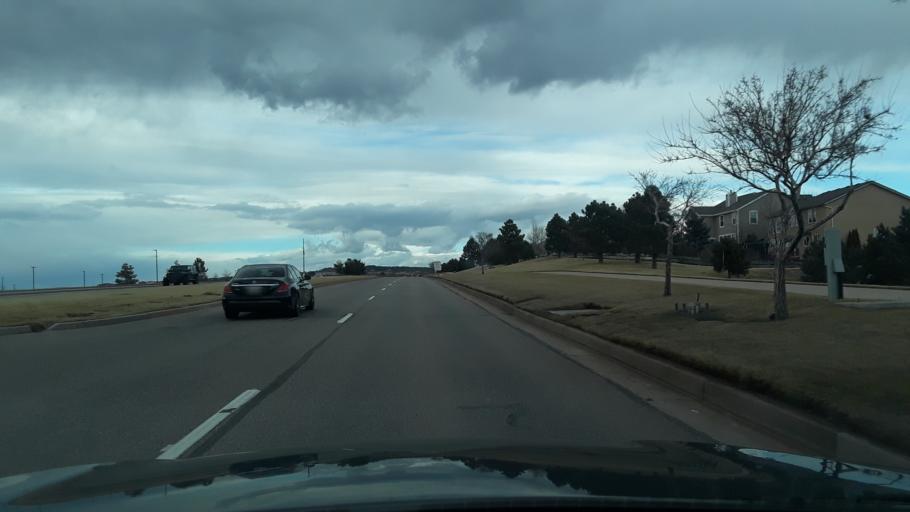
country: US
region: Colorado
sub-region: El Paso County
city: Gleneagle
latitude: 39.0129
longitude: -104.8089
